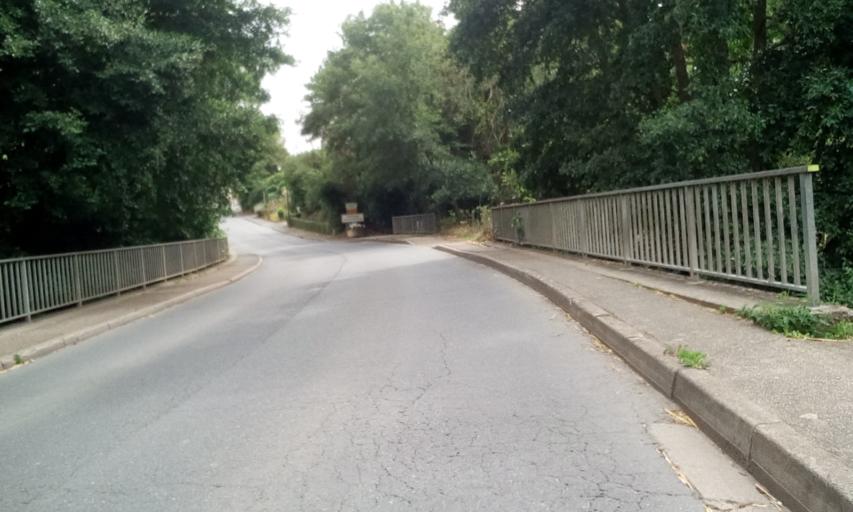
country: FR
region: Lower Normandy
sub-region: Departement du Calvados
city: Fontaine-Etoupefour
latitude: 49.1498
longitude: -0.4564
